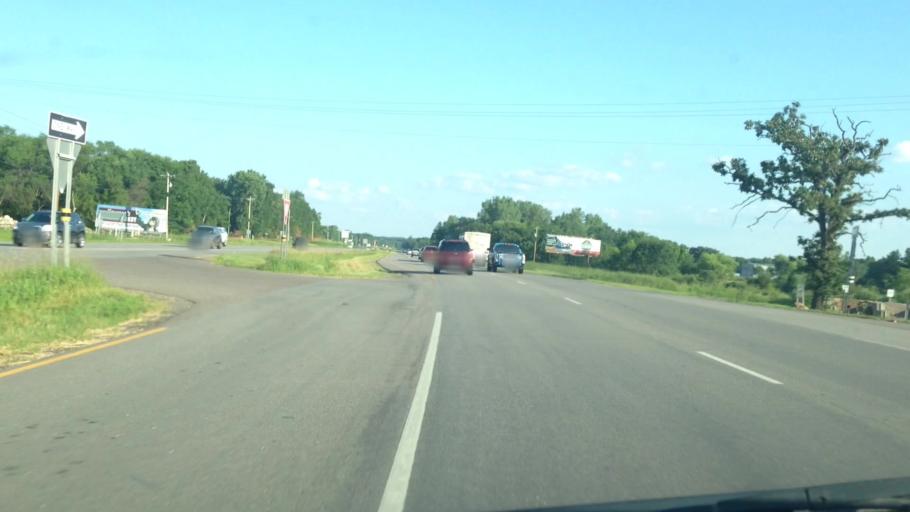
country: US
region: Minnesota
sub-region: Sherburne County
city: Zimmerman
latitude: 45.4382
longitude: -93.5823
